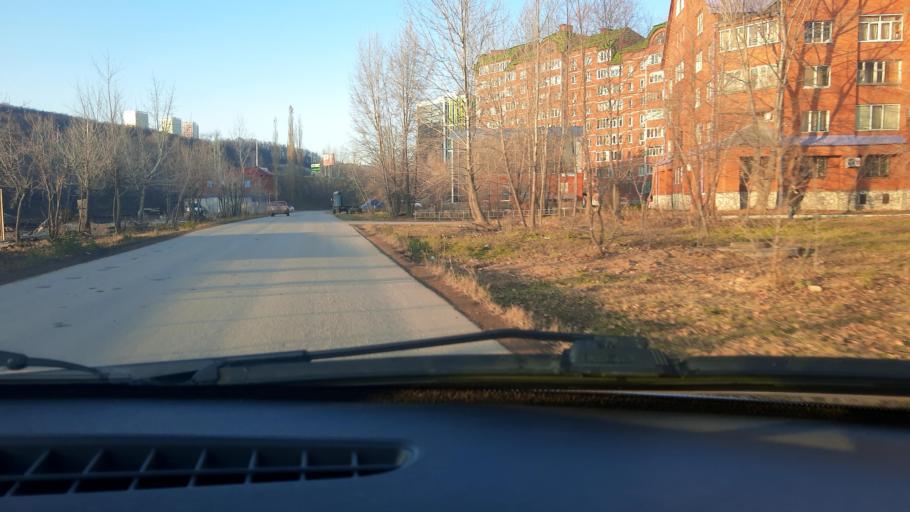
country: RU
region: Bashkortostan
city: Ufa
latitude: 54.7621
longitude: 56.0481
